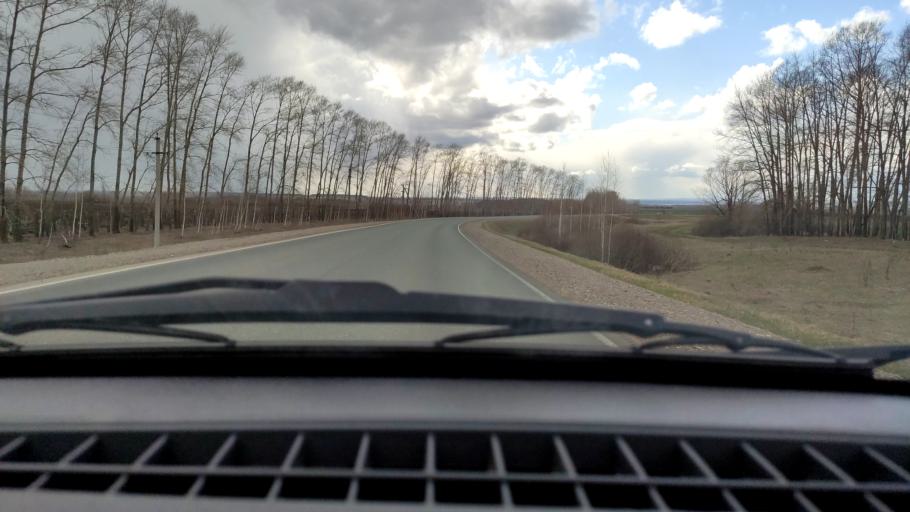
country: RU
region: Bashkortostan
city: Kushnarenkovo
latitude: 55.0581
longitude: 55.1763
